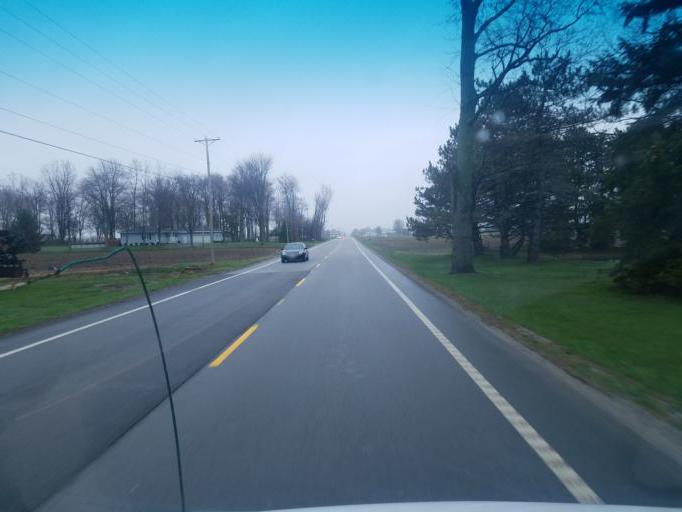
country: US
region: Ohio
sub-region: Wood County
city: Weston
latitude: 41.3721
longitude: -83.7941
